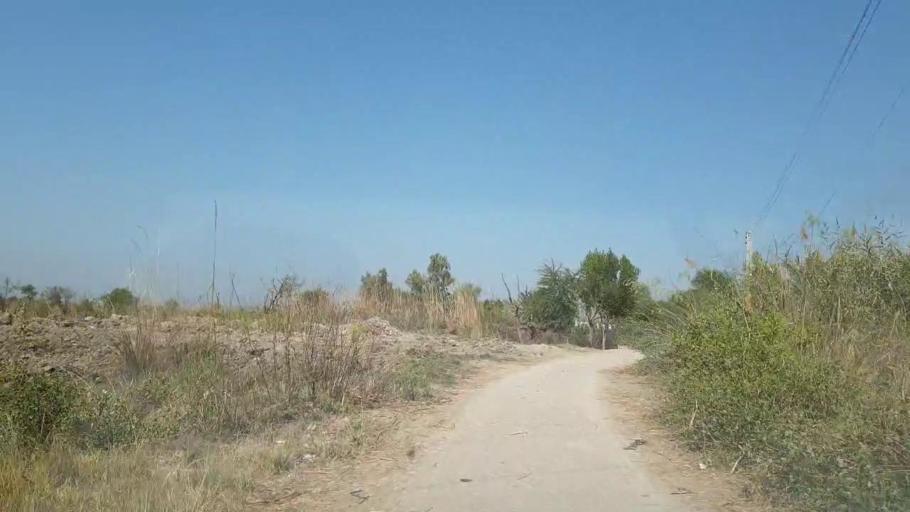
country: PK
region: Sindh
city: Mirpur Khas
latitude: 25.7238
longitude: 69.1172
